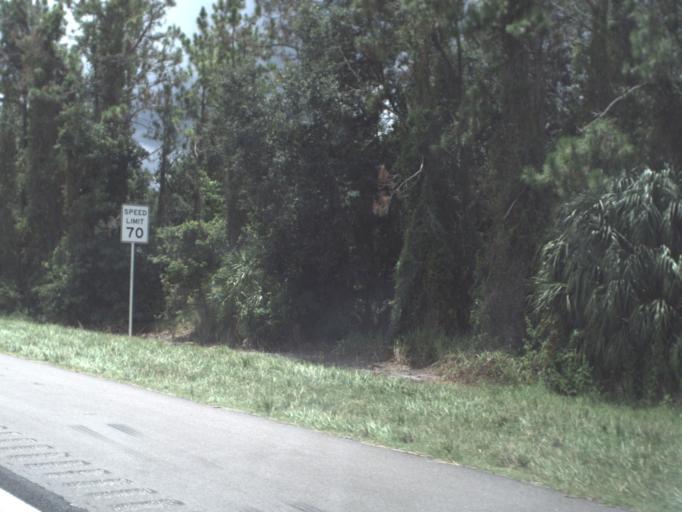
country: US
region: Florida
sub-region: Hillsborough County
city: Pebble Creek
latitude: 28.1635
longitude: -82.3951
